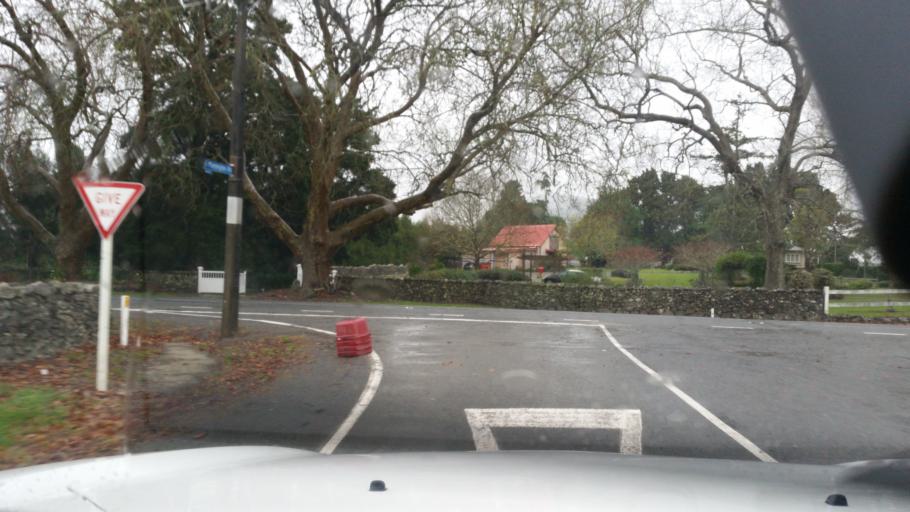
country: NZ
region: Northland
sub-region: Whangarei
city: Maungatapere
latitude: -35.7548
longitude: 174.1832
